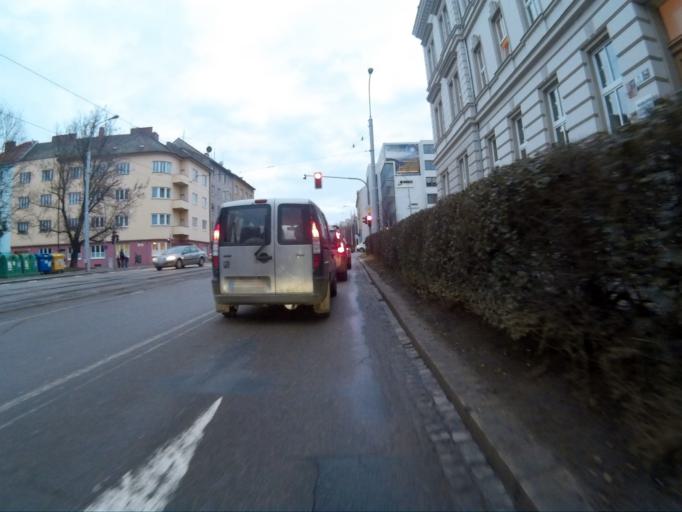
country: CZ
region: South Moravian
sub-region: Mesto Brno
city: Brno
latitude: 49.1831
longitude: 16.5950
